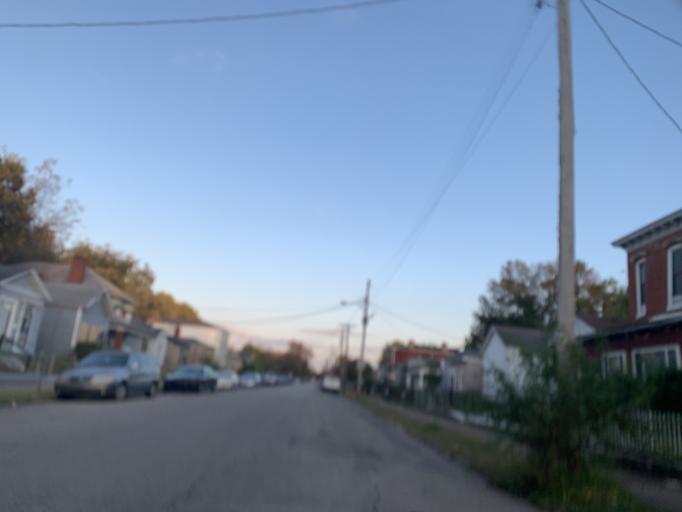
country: US
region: Kentucky
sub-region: Jefferson County
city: Louisville
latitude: 38.2530
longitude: -85.7843
